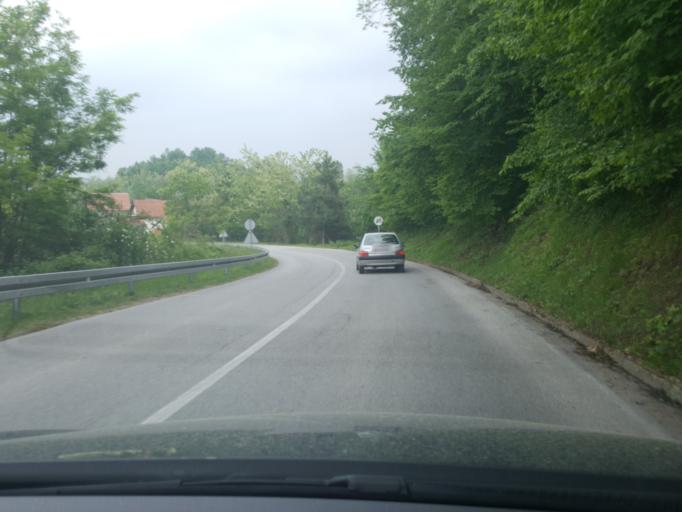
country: RS
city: Kamenica
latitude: 44.2064
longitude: 19.7172
